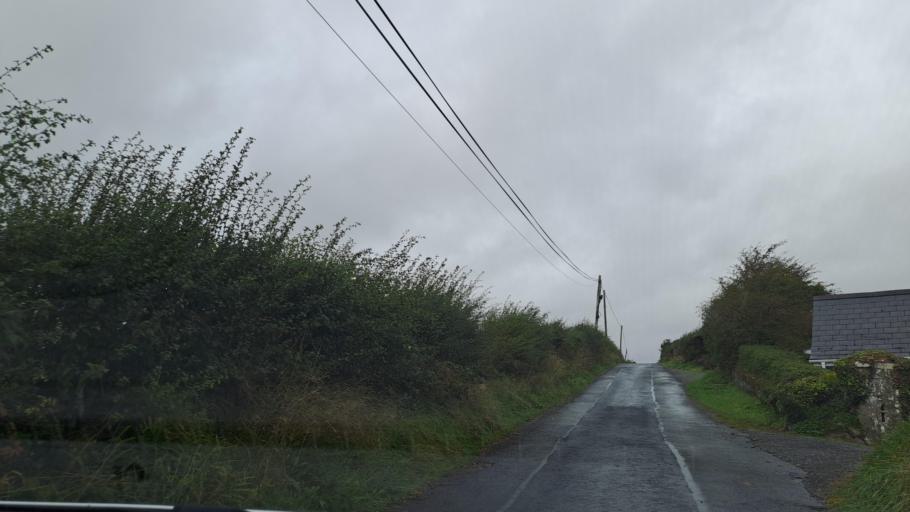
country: IE
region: Ulster
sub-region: An Cabhan
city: Kingscourt
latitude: 53.9368
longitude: -6.8628
